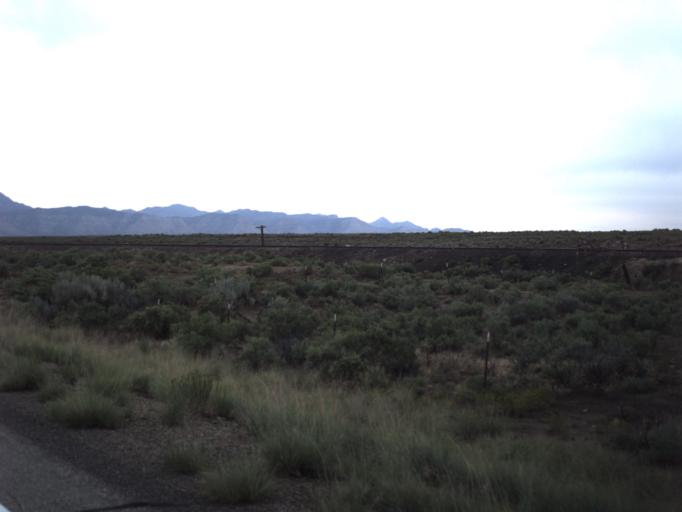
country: US
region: Utah
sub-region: Carbon County
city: East Carbon City
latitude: 39.5313
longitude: -110.5522
